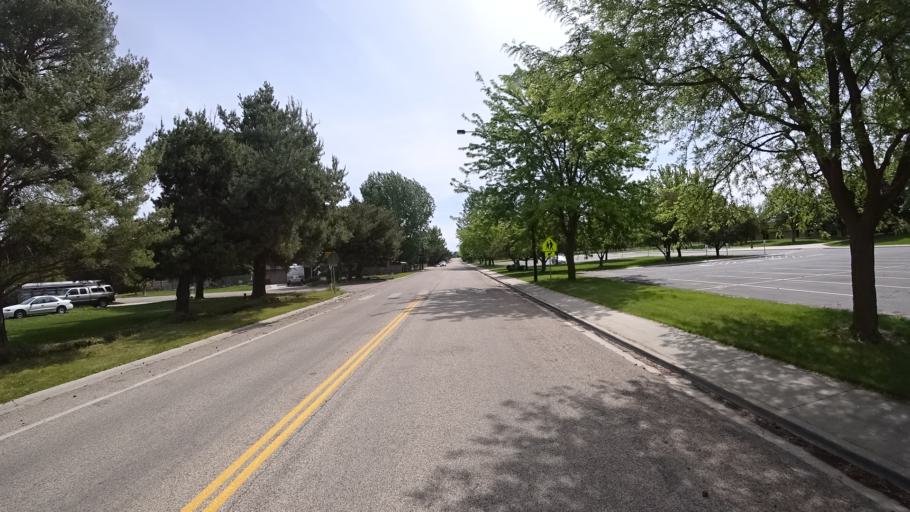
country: US
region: Idaho
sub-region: Ada County
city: Meridian
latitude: 43.5539
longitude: -116.3274
